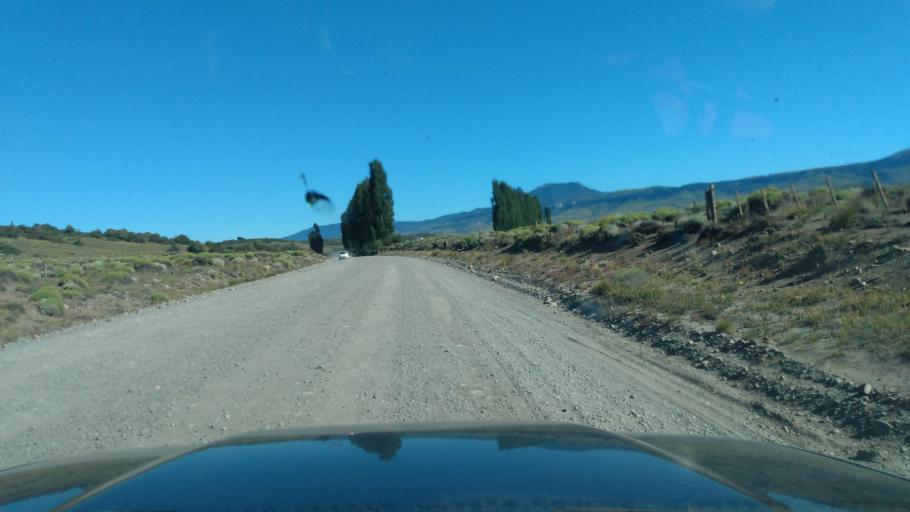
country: AR
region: Neuquen
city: Junin de los Andes
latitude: -39.8324
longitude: -71.1909
